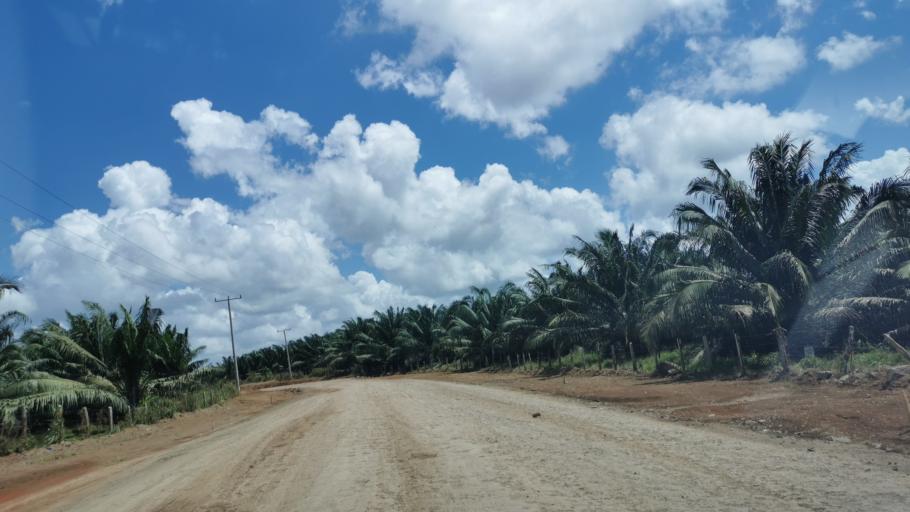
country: NI
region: Atlantico Sur
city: Rama
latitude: 12.2122
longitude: -84.2437
